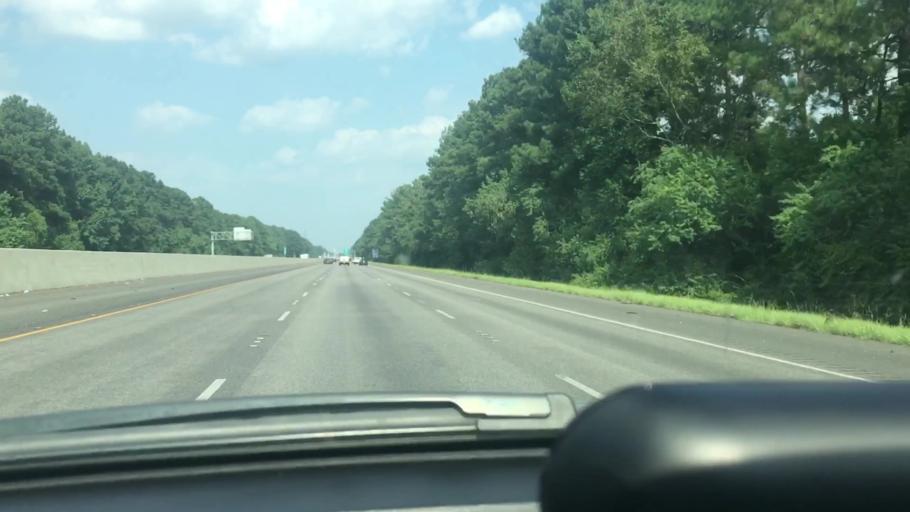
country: US
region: Louisiana
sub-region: Livingston Parish
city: Walker
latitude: 30.4689
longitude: -90.8838
